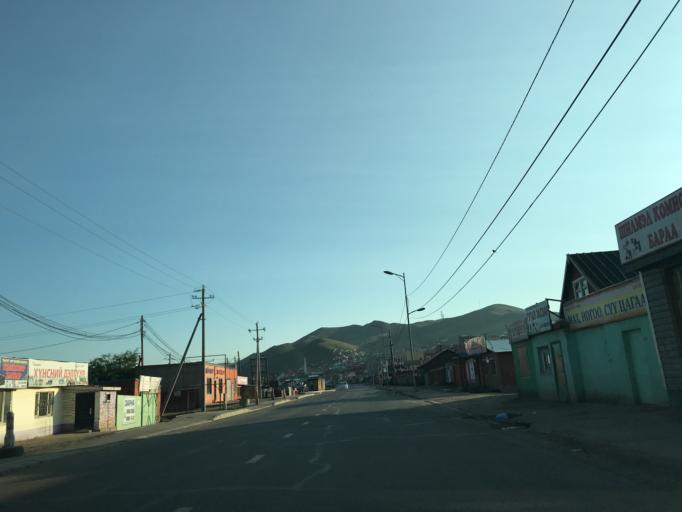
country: MN
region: Ulaanbaatar
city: Ulaanbaatar
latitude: 47.9498
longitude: 106.9325
